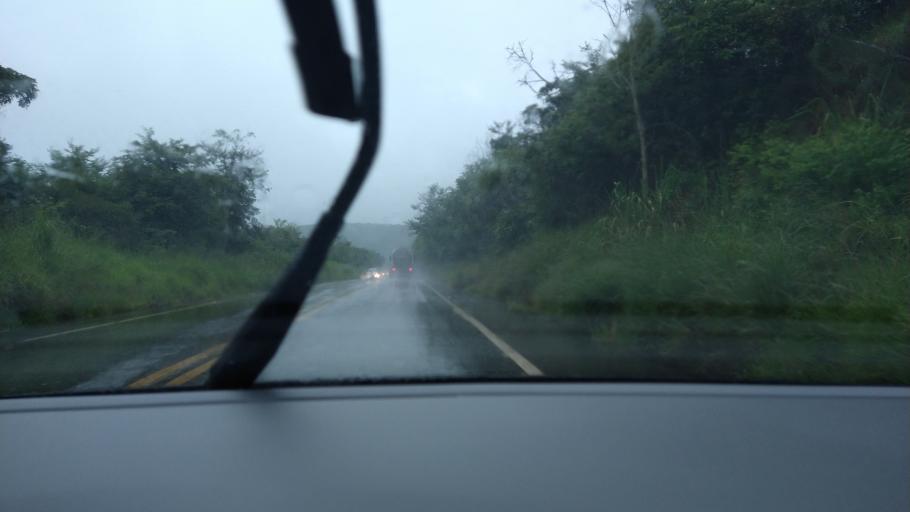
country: BR
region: Minas Gerais
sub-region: Ponte Nova
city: Ponte Nova
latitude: -20.5437
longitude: -42.8871
